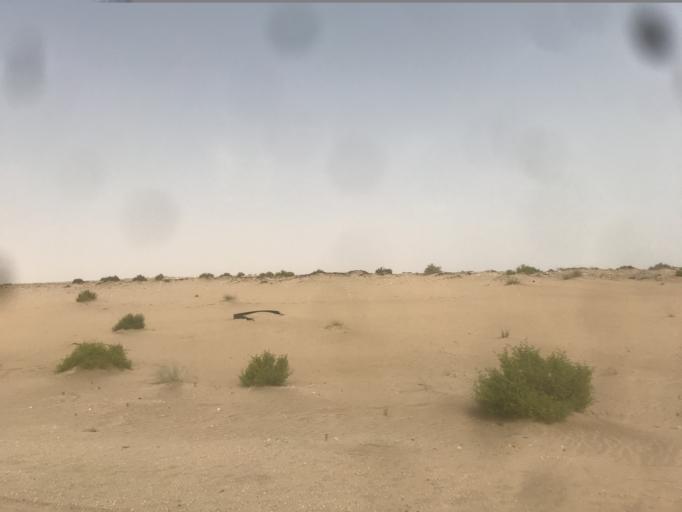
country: SA
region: Eastern Province
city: Abqaiq
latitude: 25.9105
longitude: 49.9498
